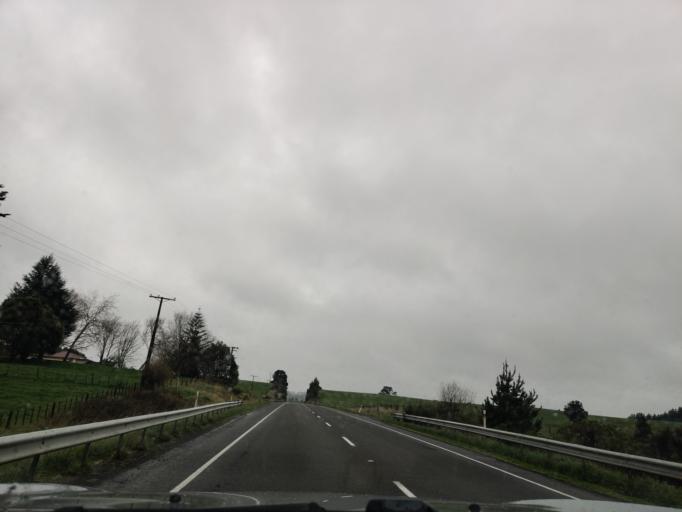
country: NZ
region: Manawatu-Wanganui
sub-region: Palmerston North City
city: Palmerston North
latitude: -40.0615
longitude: 176.2257
